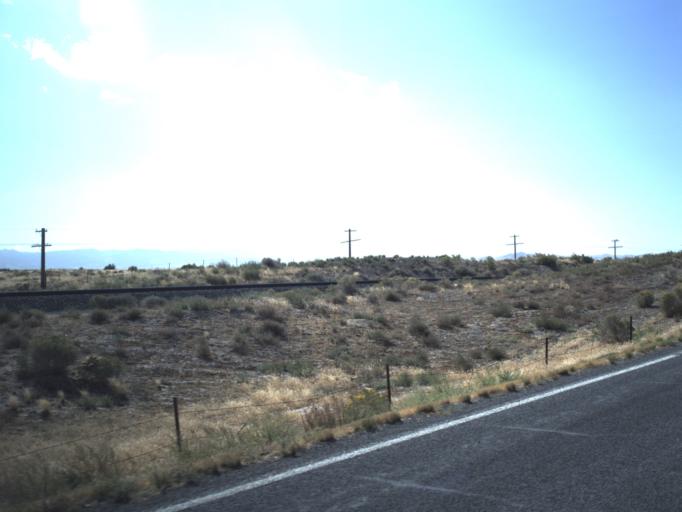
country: US
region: Utah
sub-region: Millard County
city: Delta
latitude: 38.9504
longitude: -112.8061
